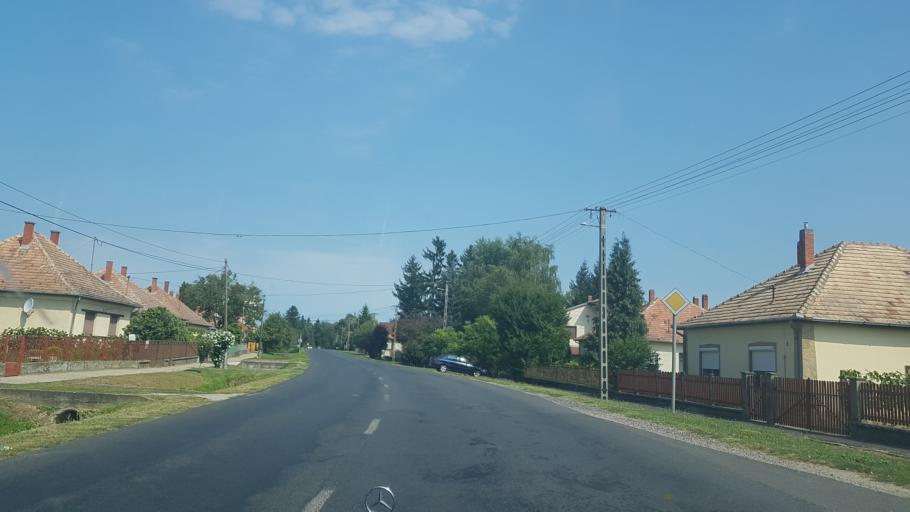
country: HU
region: Somogy
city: Bohonye
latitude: 46.4929
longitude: 17.4241
